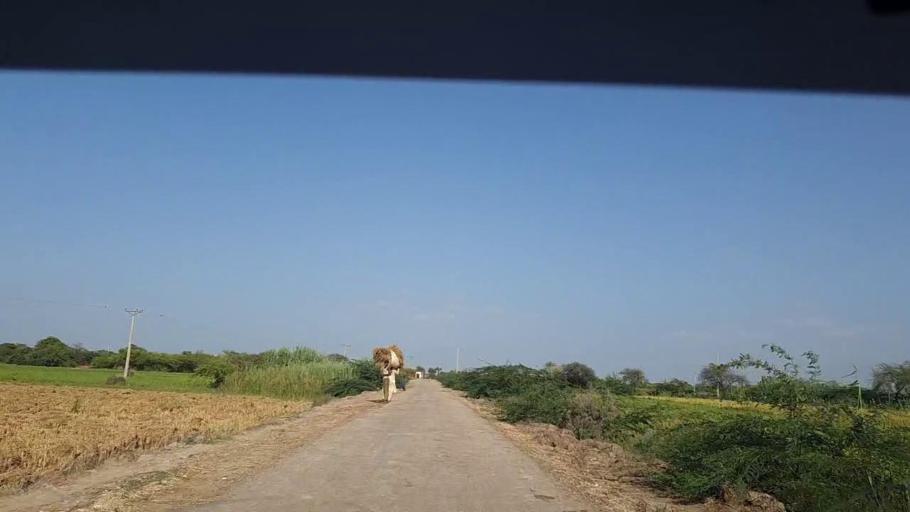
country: PK
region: Sindh
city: Kadhan
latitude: 24.4637
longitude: 68.8492
